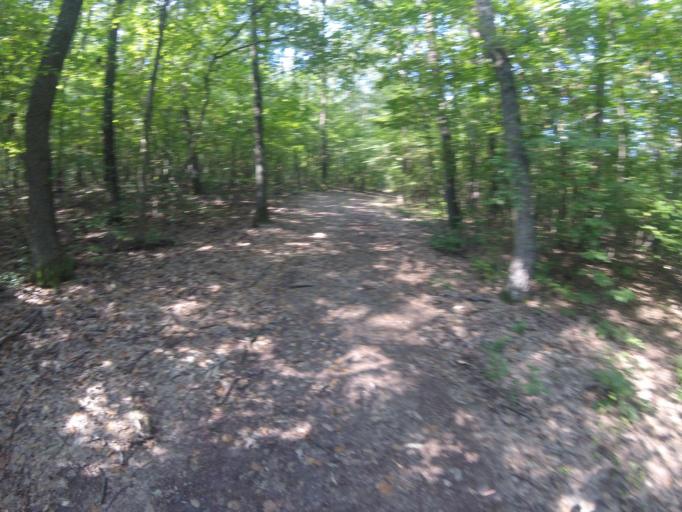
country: HU
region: Nograd
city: Bujak
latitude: 47.8961
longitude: 19.5246
